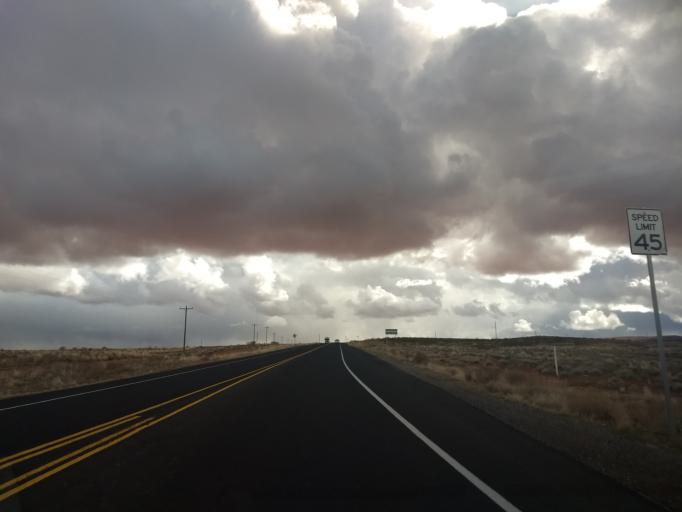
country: US
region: Utah
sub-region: Washington County
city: Hurricane
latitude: 37.1473
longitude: -113.3897
